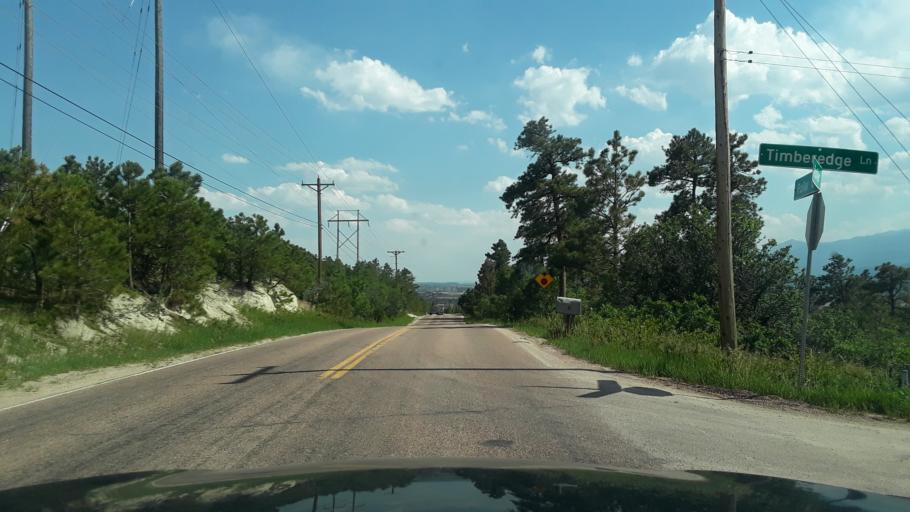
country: US
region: Colorado
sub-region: El Paso County
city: Gleneagle
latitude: 39.0384
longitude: -104.7849
